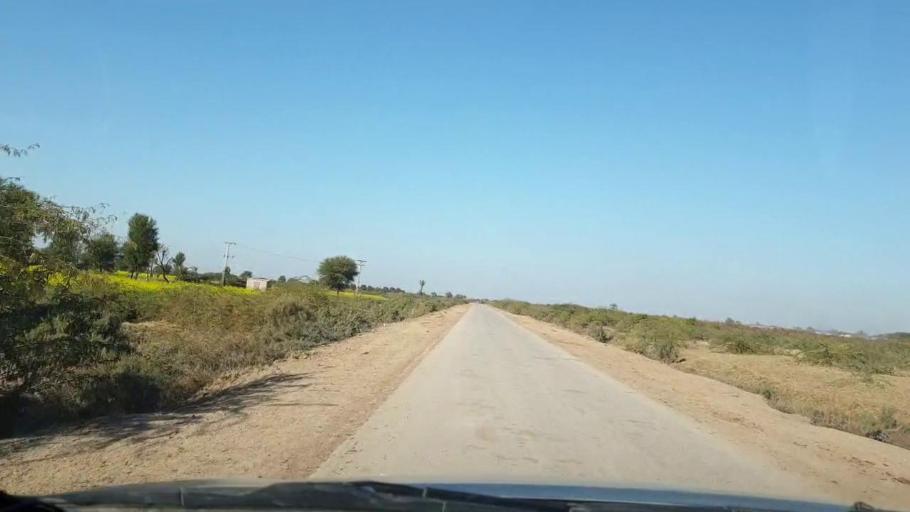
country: PK
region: Sindh
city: Jhol
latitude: 25.8358
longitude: 68.9513
